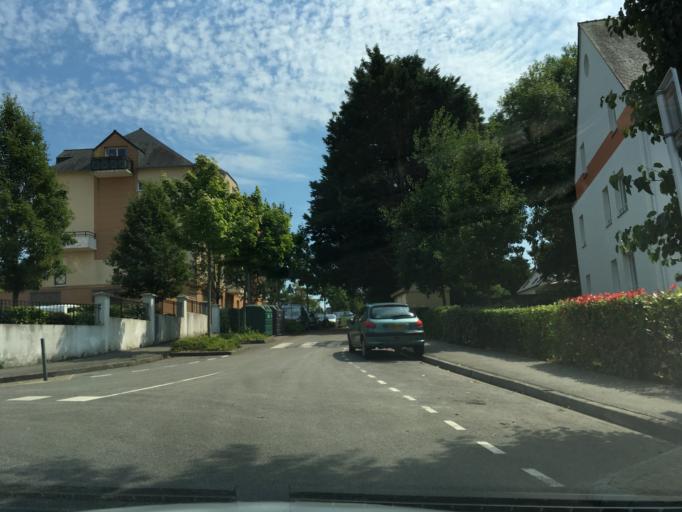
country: FR
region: Brittany
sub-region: Departement du Morbihan
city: Lorient
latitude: 47.7536
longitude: -3.3973
